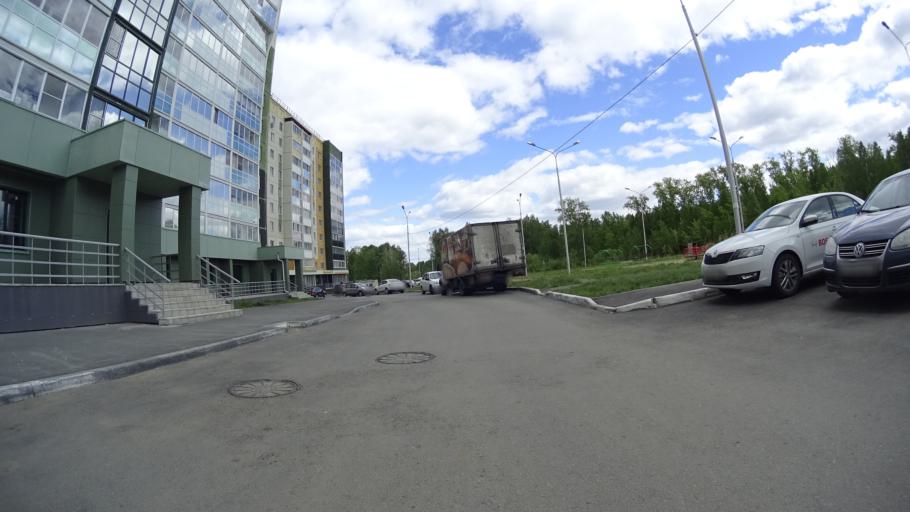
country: RU
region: Chelyabinsk
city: Roshchino
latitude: 55.1721
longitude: 61.2581
